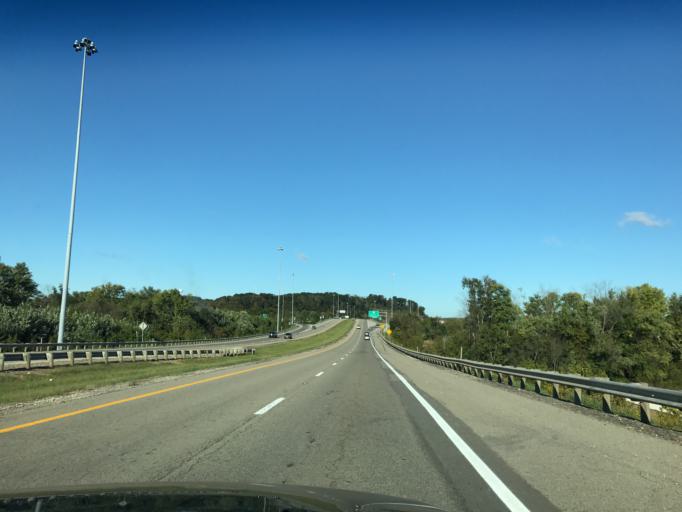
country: US
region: West Virginia
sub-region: Wood County
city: Parkersburg
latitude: 39.2566
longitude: -81.5486
